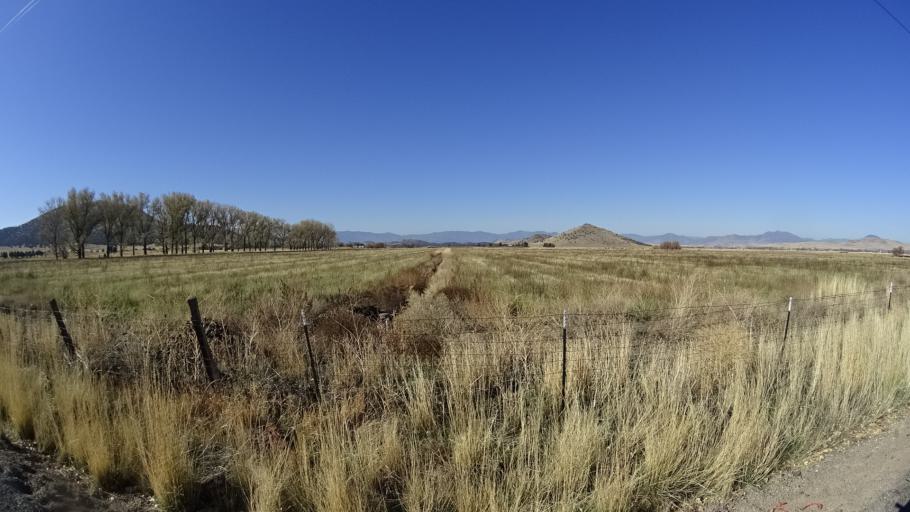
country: US
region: California
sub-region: Siskiyou County
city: Montague
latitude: 41.6856
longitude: -122.3697
